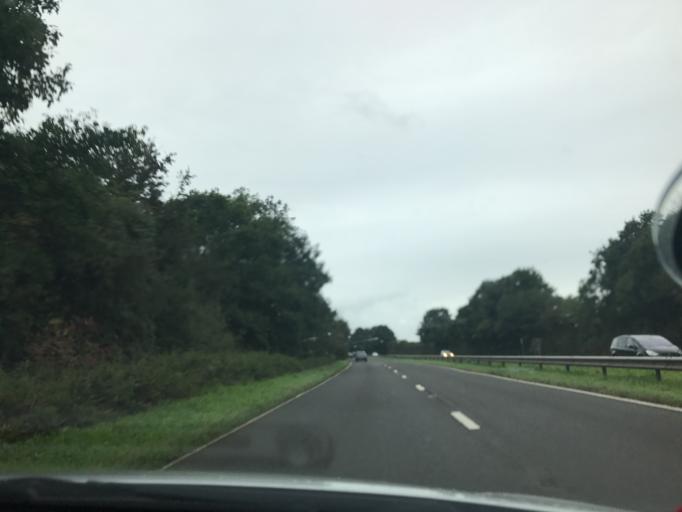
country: GB
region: England
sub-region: Cheshire West and Chester
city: Hartford
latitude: 53.2381
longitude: -2.5613
